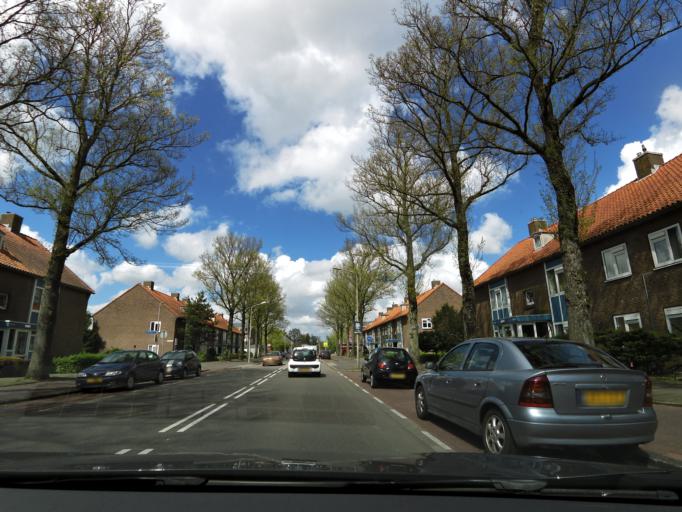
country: NL
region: North Holland
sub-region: Gemeente Amstelveen
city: Amstelveen
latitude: 52.2957
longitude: 4.8547
